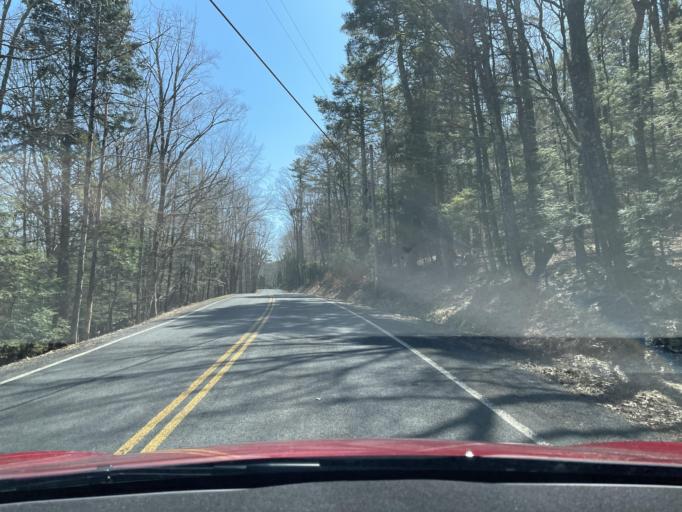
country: US
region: New York
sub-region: Ulster County
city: Shokan
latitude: 42.0143
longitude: -74.1719
